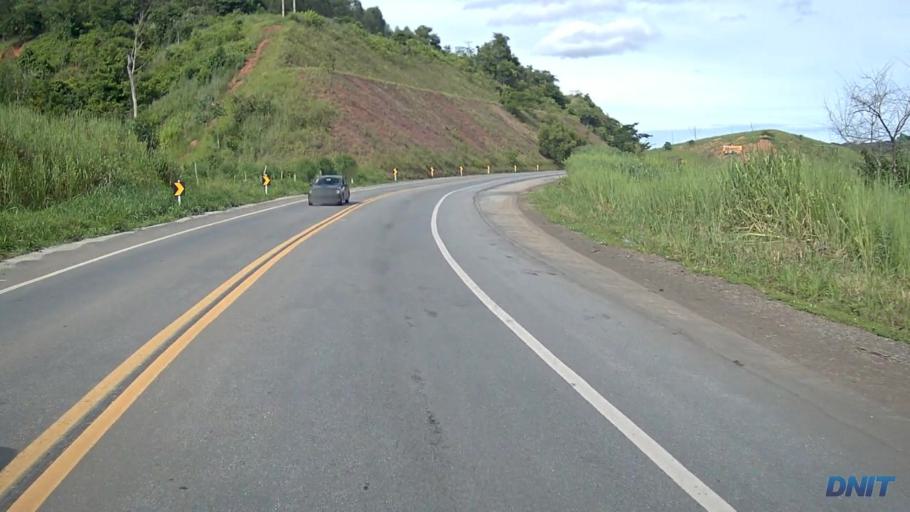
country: BR
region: Minas Gerais
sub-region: Belo Oriente
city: Belo Oriente
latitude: -19.2655
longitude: -42.3518
